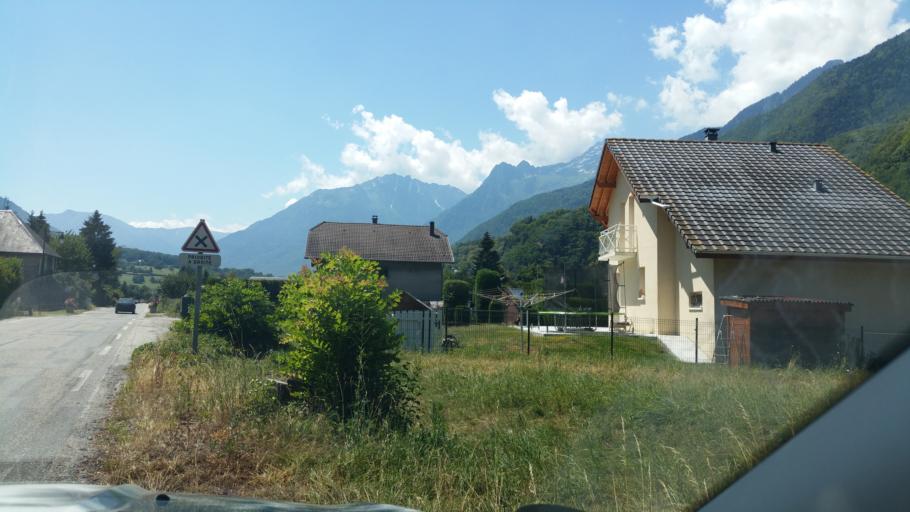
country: FR
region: Rhone-Alpes
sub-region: Departement de la Savoie
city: Saint-Remy-de-Maurienne
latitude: 45.4439
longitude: 6.2818
